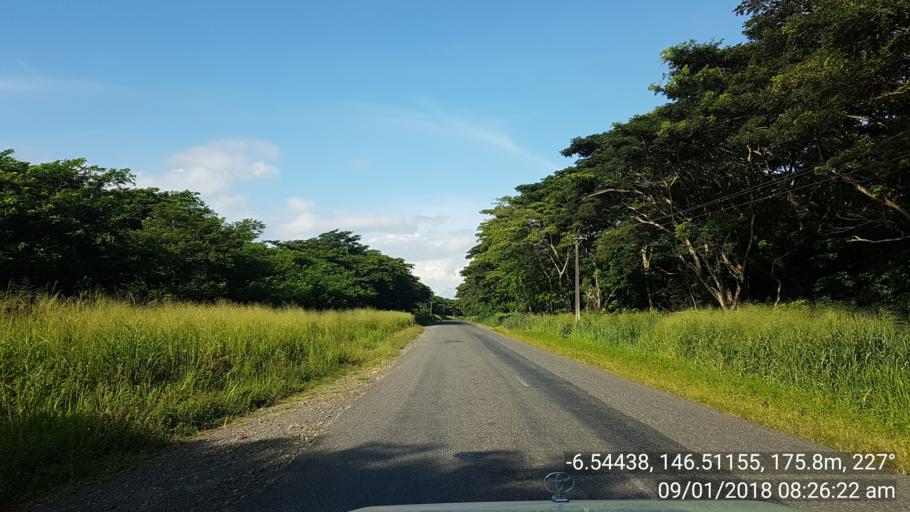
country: PG
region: Morobe
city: Lae
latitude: -6.5444
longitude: 146.5117
